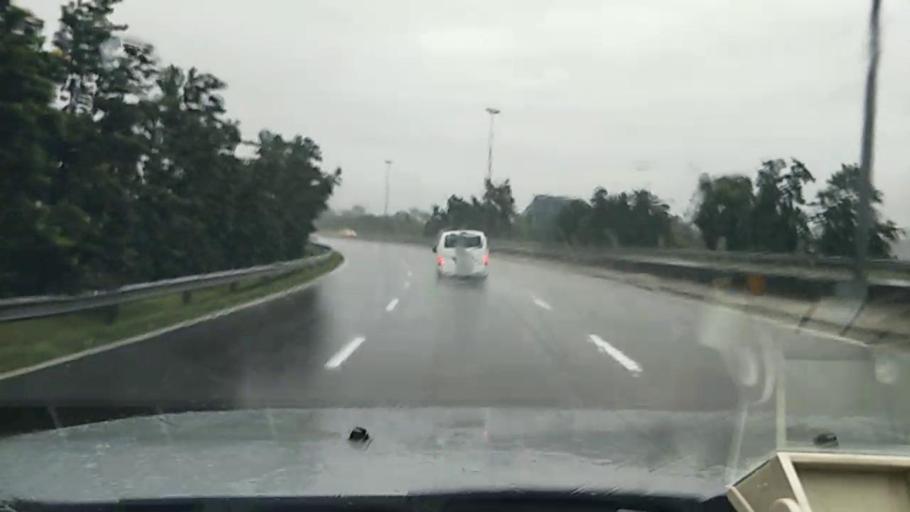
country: MY
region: Selangor
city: Kampong Baharu Balakong
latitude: 2.9988
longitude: 101.7752
